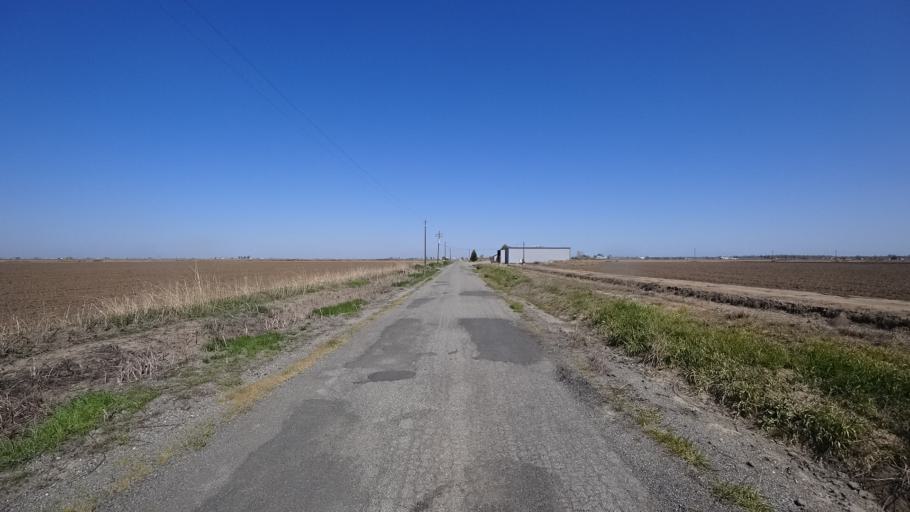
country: US
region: California
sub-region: Glenn County
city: Willows
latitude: 39.4260
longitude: -122.0464
